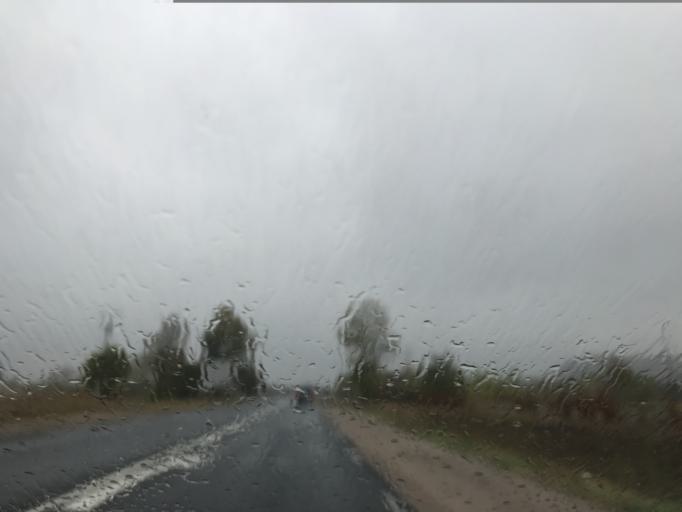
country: FR
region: Auvergne
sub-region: Departement du Puy-de-Dome
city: Pont-du-Chateau
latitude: 45.7857
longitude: 3.2551
